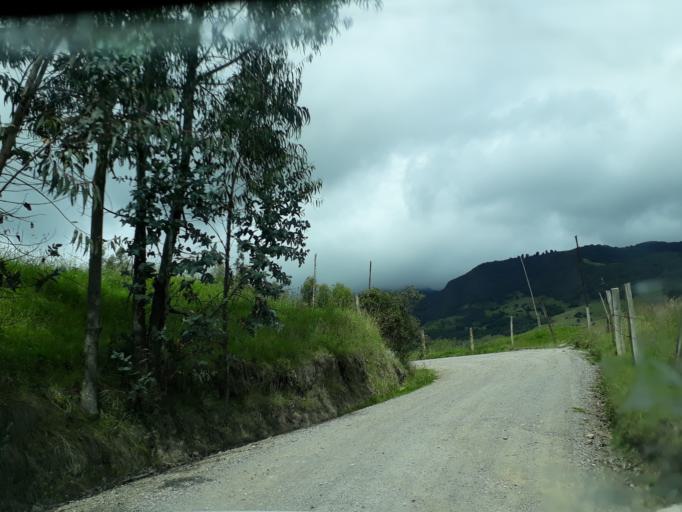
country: CO
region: Cundinamarca
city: La Mesa
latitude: 5.2787
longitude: -73.9074
